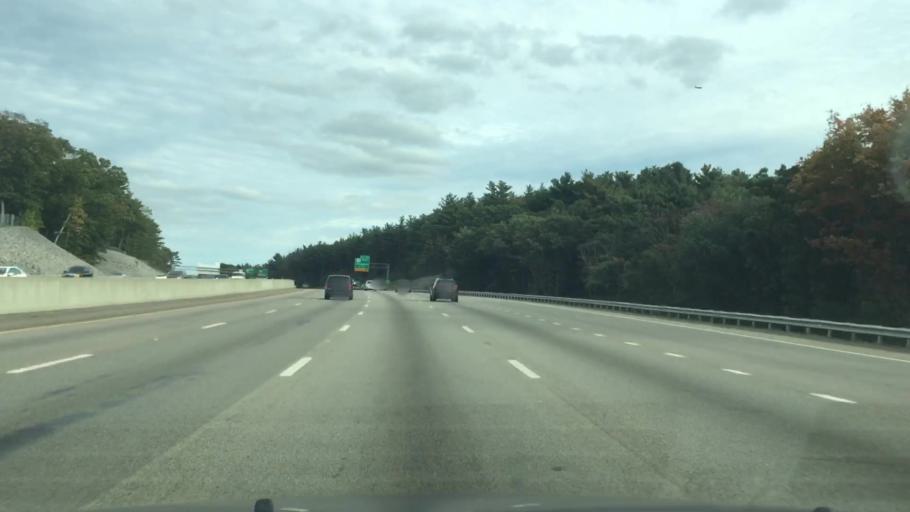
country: US
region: Massachusetts
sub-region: Norfolk County
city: Canton
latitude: 42.2037
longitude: -71.1318
